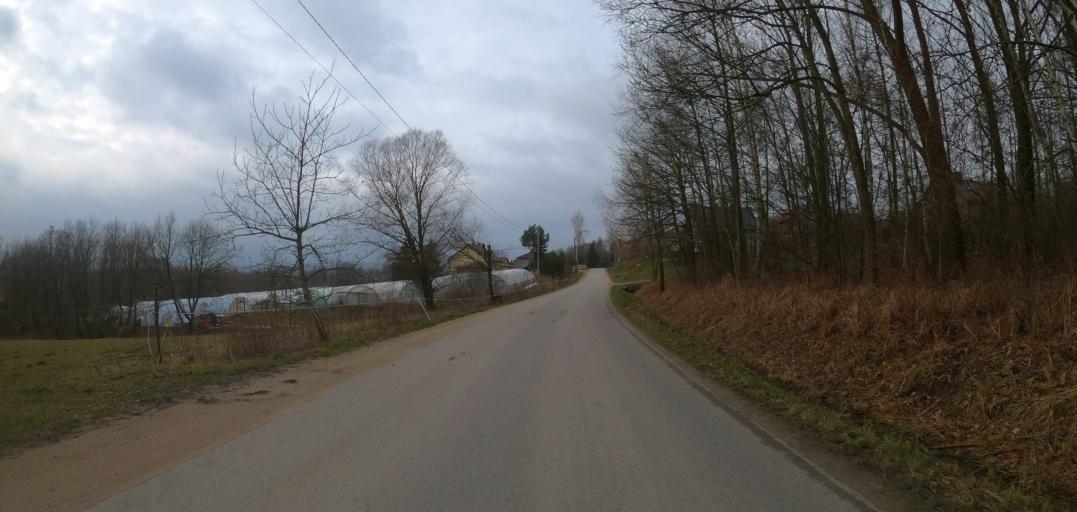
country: PL
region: Subcarpathian Voivodeship
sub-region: Powiat debicki
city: Pilzno
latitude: 49.9885
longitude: 21.3315
